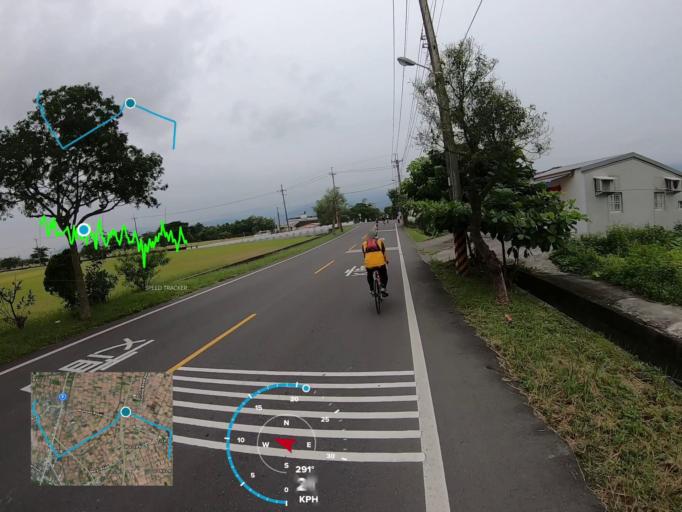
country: TW
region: Taiwan
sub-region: Yilan
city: Yilan
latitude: 24.7834
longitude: 121.7762
